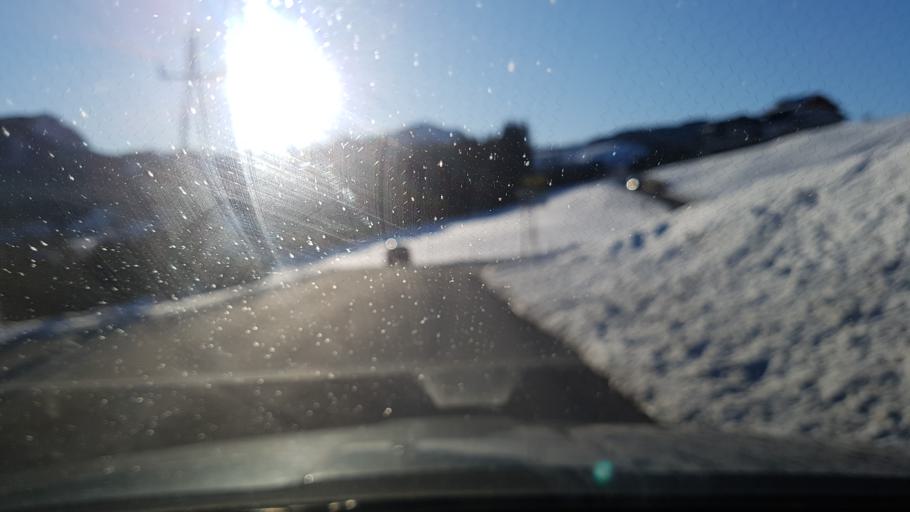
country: AT
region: Salzburg
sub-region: Politischer Bezirk Hallein
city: Golling an der Salzach
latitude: 47.6522
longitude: 13.2058
